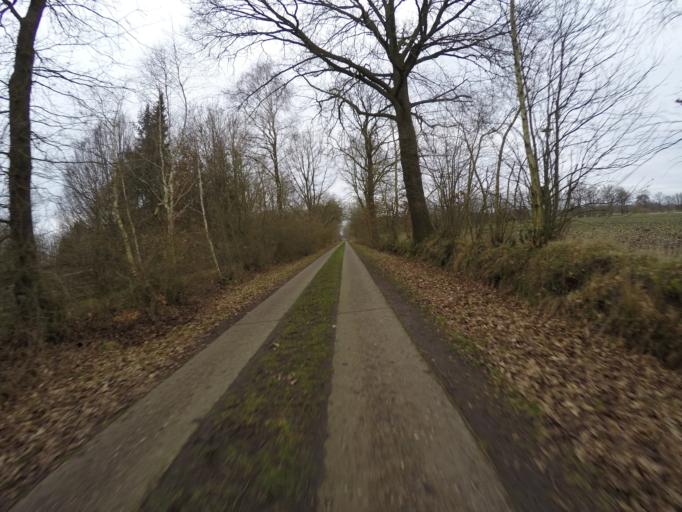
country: DE
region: Schleswig-Holstein
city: Hemdingen
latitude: 53.7735
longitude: 9.8420
